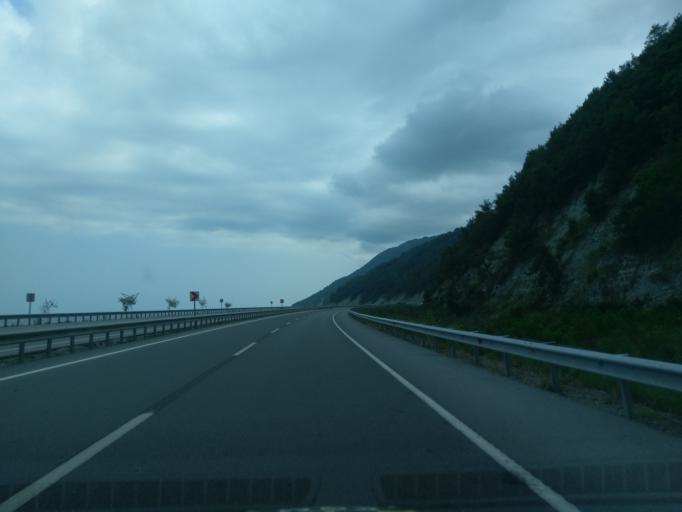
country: TR
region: Sinop
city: Dikmen
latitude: 41.7081
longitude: 35.3017
